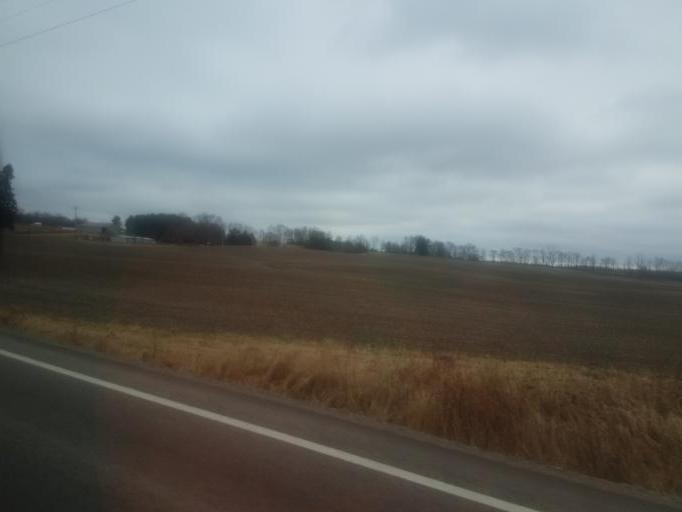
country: US
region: Ohio
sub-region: Knox County
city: Fredericktown
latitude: 40.5198
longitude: -82.6682
